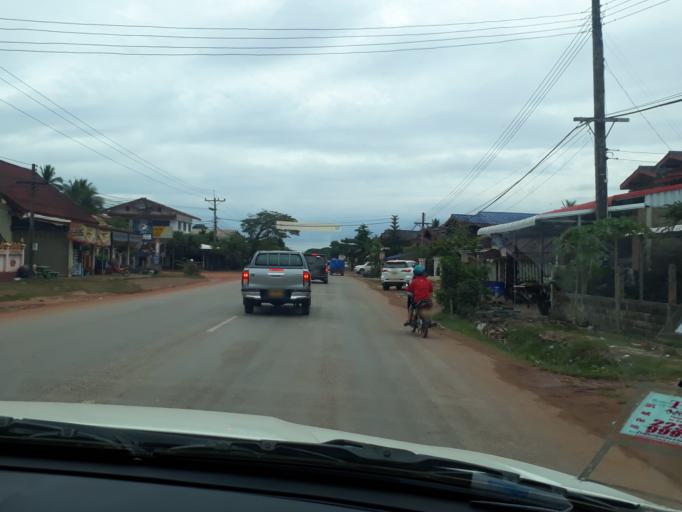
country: LA
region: Vientiane
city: Muang Phon-Hong
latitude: 18.3411
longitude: 102.4324
